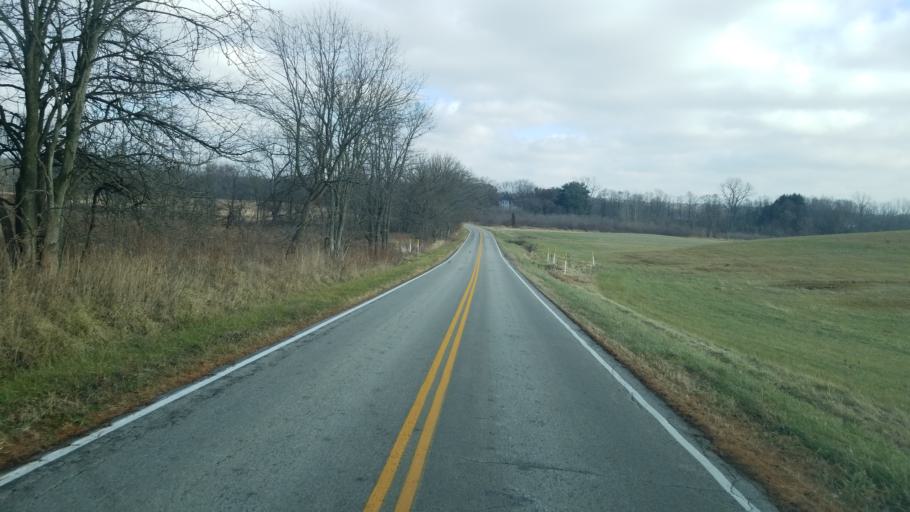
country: US
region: Ohio
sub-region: Richland County
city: Lincoln Heights
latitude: 40.8148
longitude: -82.4246
